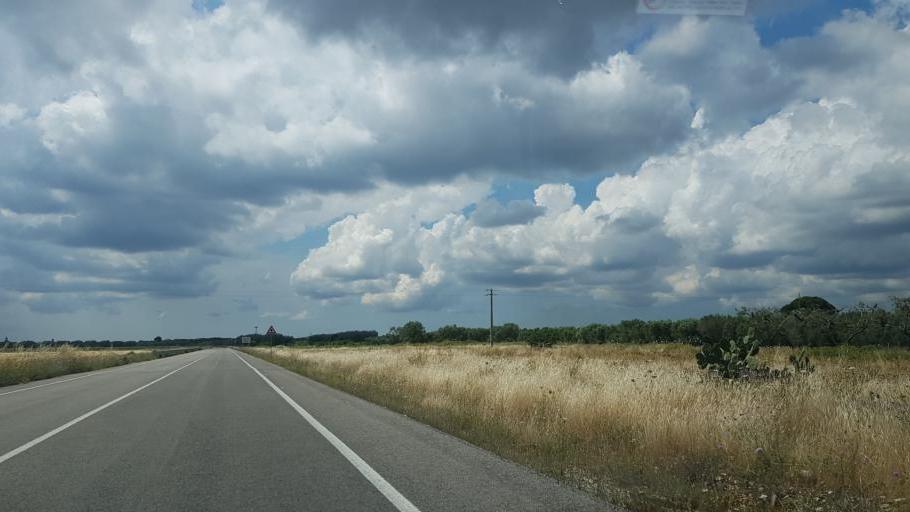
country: IT
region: Apulia
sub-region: Provincia di Brindisi
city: Mesagne
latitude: 40.5025
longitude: 17.8281
